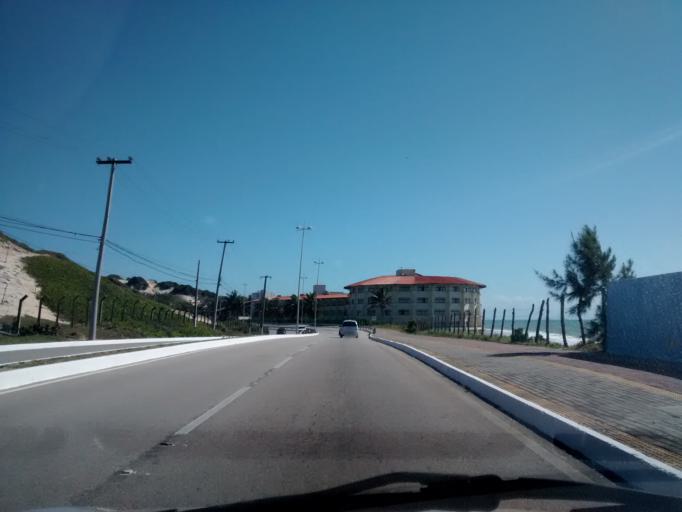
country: BR
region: Rio Grande do Norte
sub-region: Natal
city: Natal
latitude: -5.8113
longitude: -35.1819
